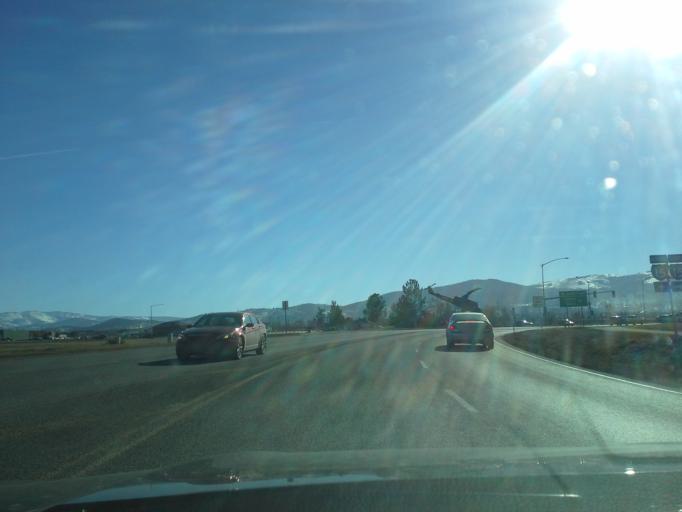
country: US
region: Montana
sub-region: Lewis and Clark County
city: Helena
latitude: 46.6076
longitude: -112.0038
